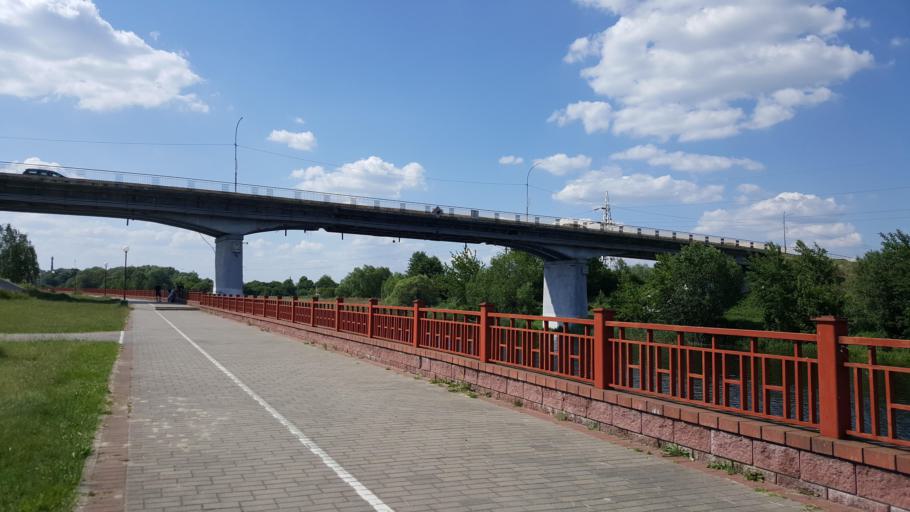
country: BY
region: Brest
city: Kobryn
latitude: 52.2151
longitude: 24.3599
